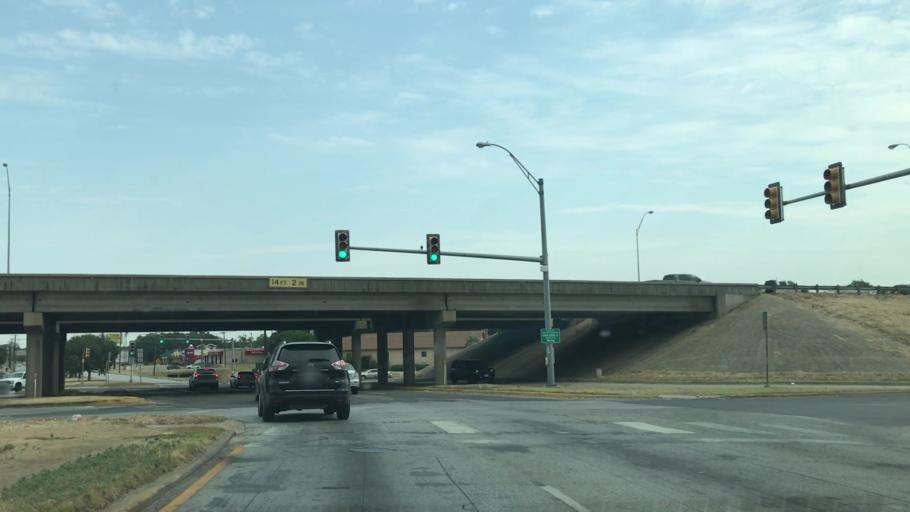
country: US
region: Texas
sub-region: Tarrant County
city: Haltom City
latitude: 32.7745
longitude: -97.2875
